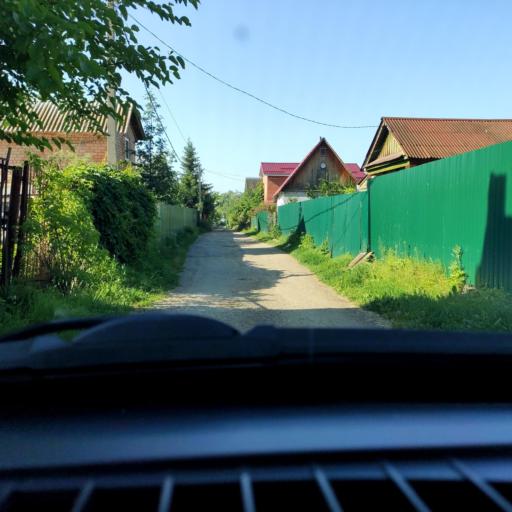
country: RU
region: Samara
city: Zhigulevsk
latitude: 53.4561
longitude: 49.5452
